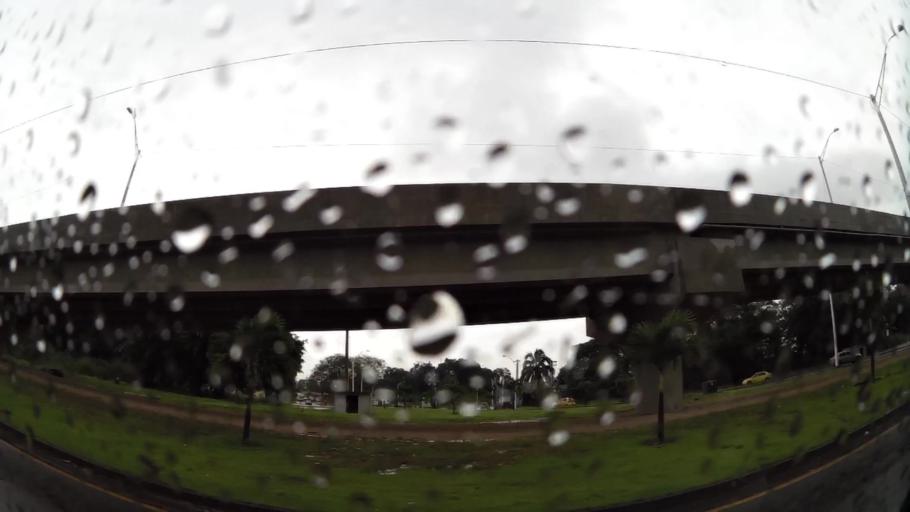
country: PA
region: Colon
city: Arco Iris
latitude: 9.3374
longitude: -79.8890
